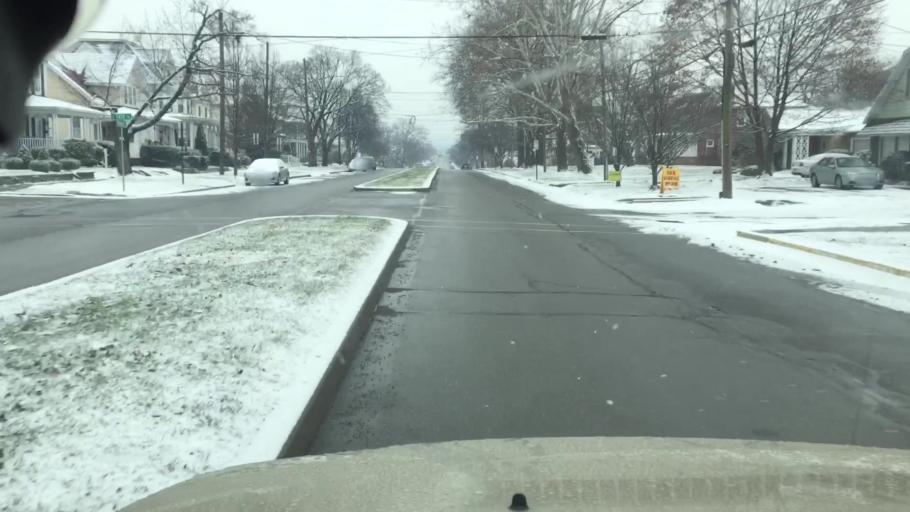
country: US
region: Pennsylvania
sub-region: Columbia County
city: Berwick
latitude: 41.0643
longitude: -76.2417
